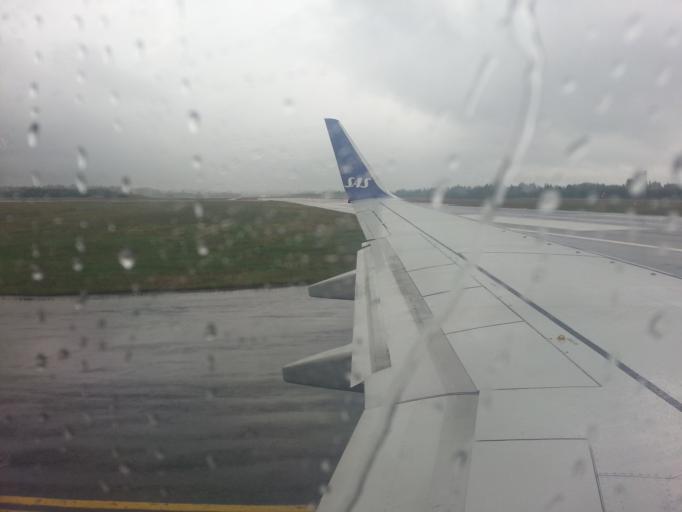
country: NO
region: Akershus
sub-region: Ullensaker
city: Jessheim
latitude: 60.1966
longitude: 11.1186
